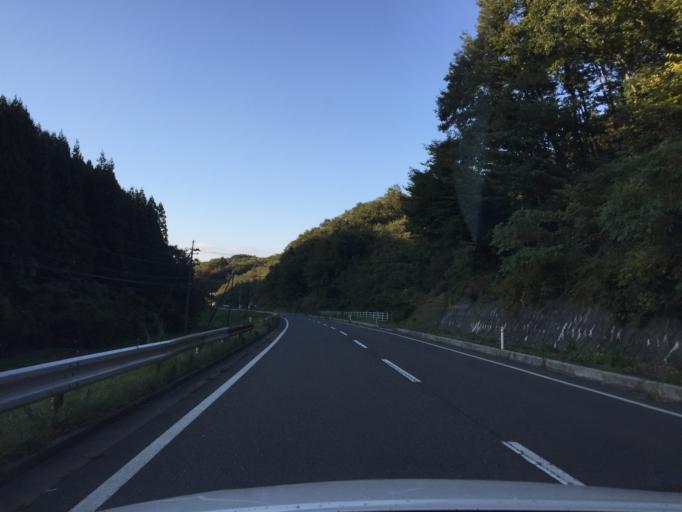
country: JP
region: Fukushima
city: Ishikawa
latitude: 37.1799
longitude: 140.6490
